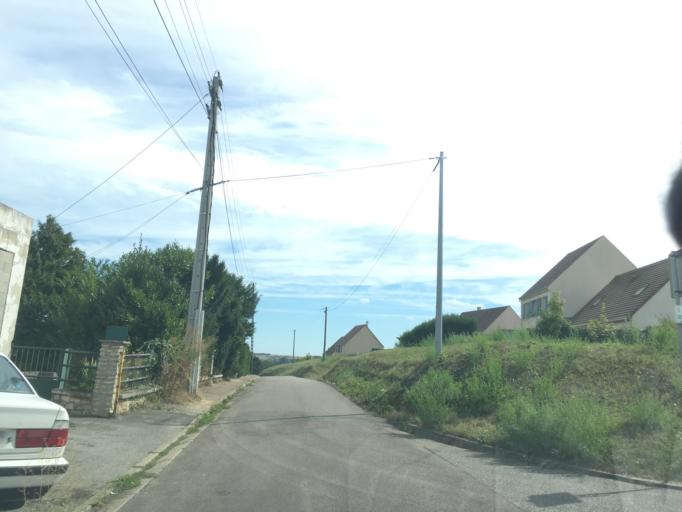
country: FR
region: Haute-Normandie
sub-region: Departement de l'Eure
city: Vernon
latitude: 49.0822
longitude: 1.5006
